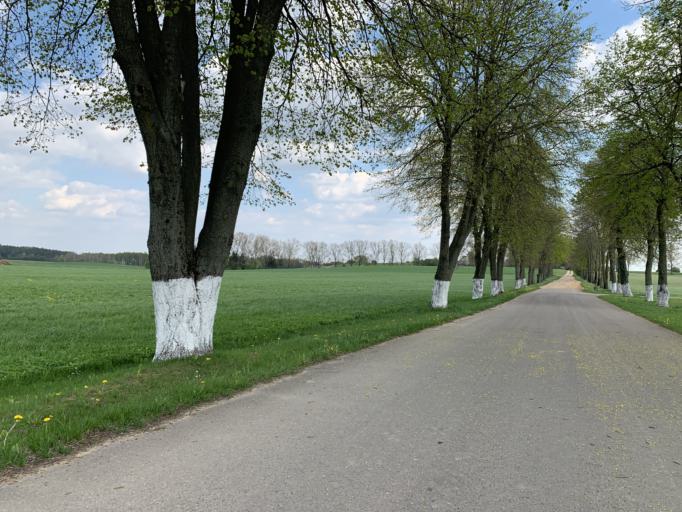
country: BY
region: Minsk
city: Nyasvizh
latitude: 53.2459
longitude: 26.6891
